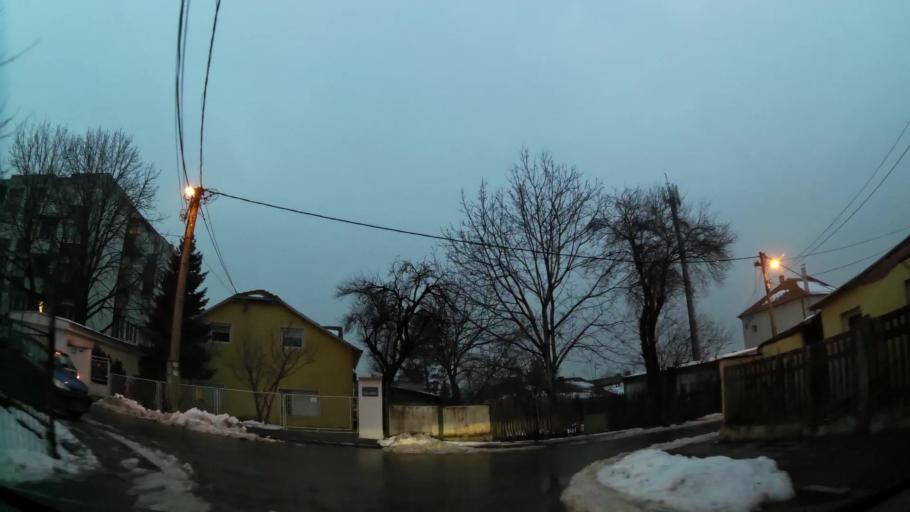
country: RS
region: Central Serbia
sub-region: Belgrade
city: Vozdovac
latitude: 44.7792
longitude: 20.4858
